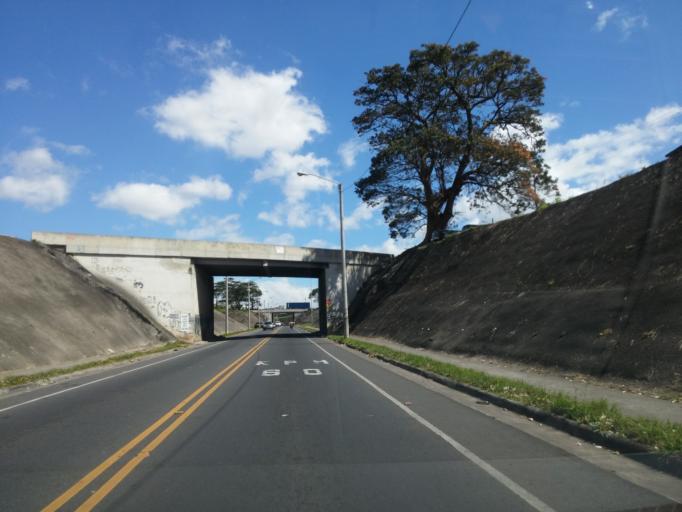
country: CR
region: San Jose
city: San Felipe
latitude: 9.9214
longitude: -84.1099
